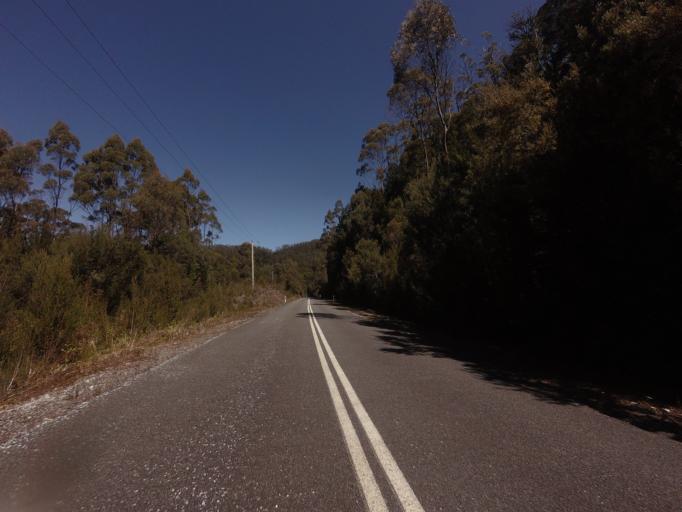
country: AU
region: Tasmania
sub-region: West Coast
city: Queenstown
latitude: -42.7643
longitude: 146.0056
